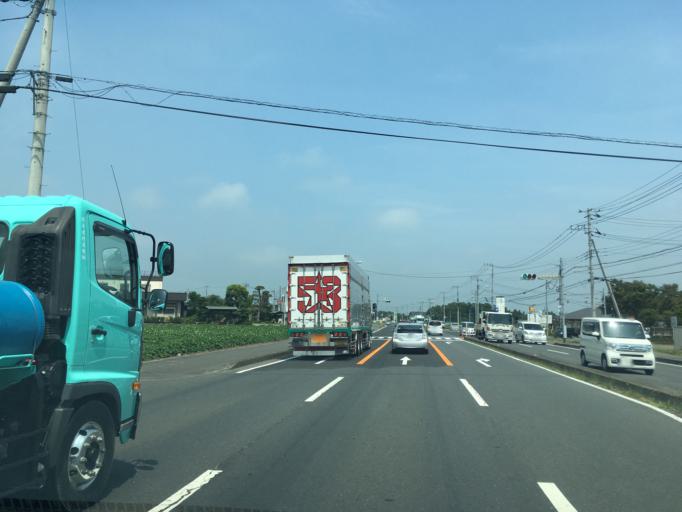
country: JP
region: Ibaraki
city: Hitachi-Naka
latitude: 36.3924
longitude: 140.5801
